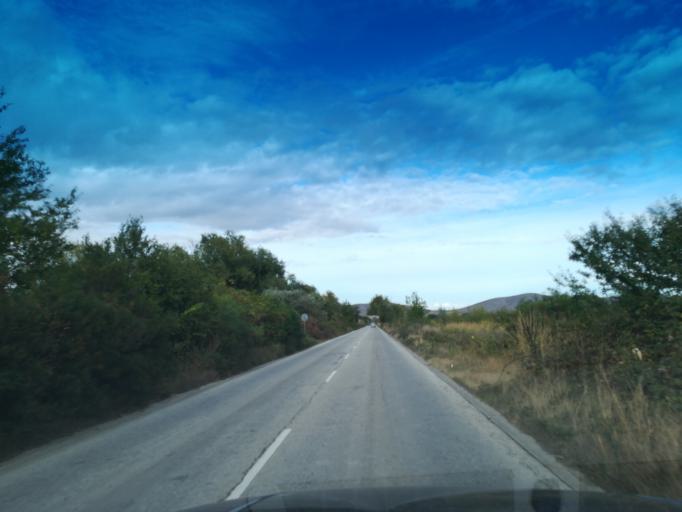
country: BG
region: Plovdiv
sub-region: Obshtina Krichim
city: Krichim
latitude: 42.0716
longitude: 24.4048
